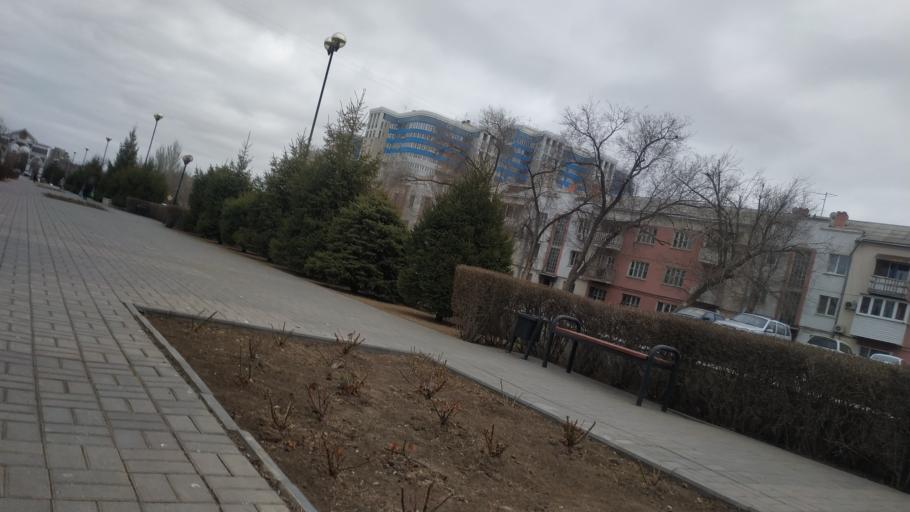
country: RU
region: Astrakhan
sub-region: Gorod Astrakhan'
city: Astrakhan'
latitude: 46.3463
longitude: 48.0177
